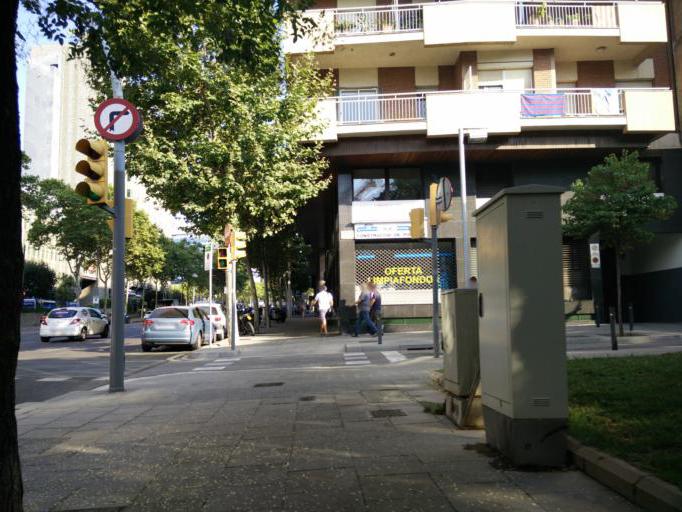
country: ES
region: Catalonia
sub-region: Provincia de Barcelona
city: les Corts
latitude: 41.3895
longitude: 2.1386
